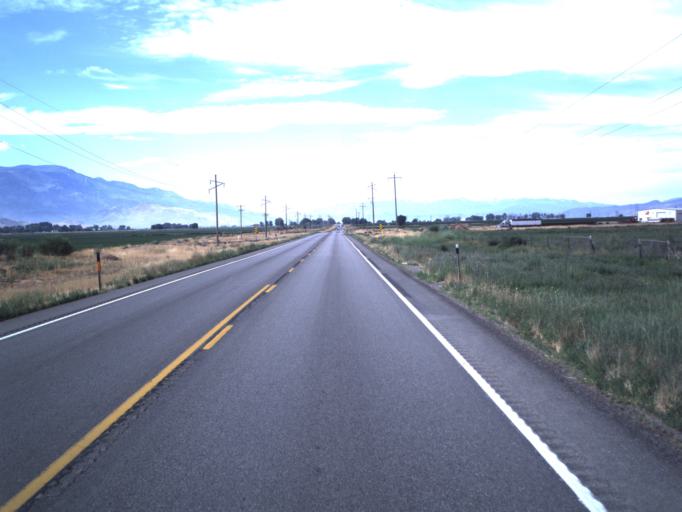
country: US
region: Utah
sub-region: Sevier County
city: Aurora
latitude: 38.8594
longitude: -111.9698
